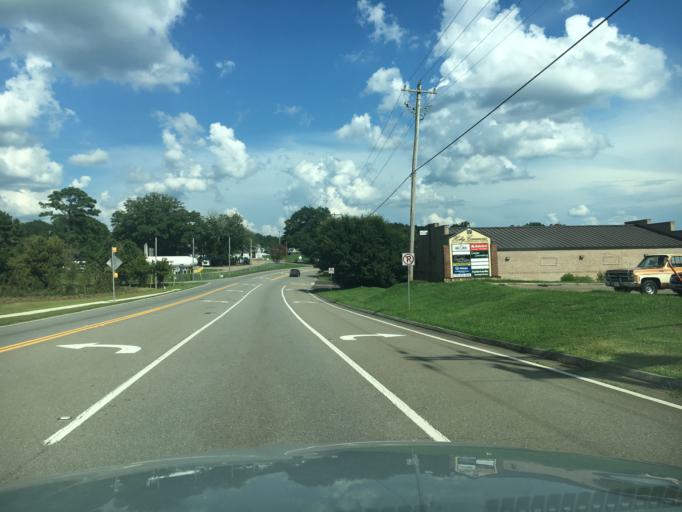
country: US
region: Georgia
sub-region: Cherokee County
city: Holly Springs
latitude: 34.1948
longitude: -84.4467
